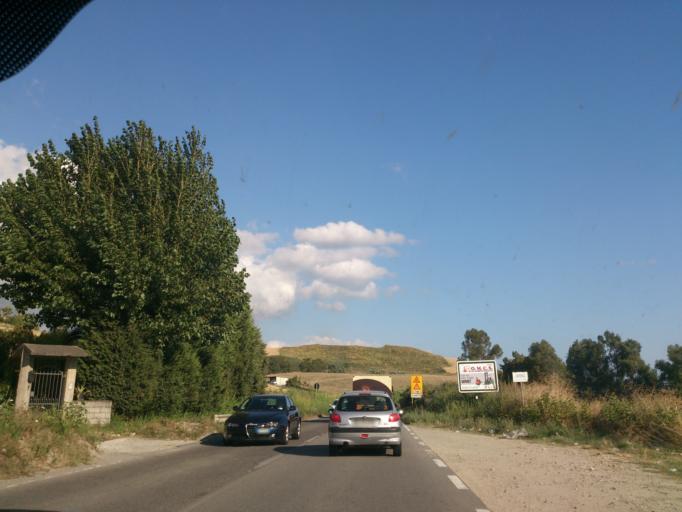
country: IT
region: Calabria
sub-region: Provincia di Catanzaro
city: Catanzaro
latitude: 38.8770
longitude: 16.5603
